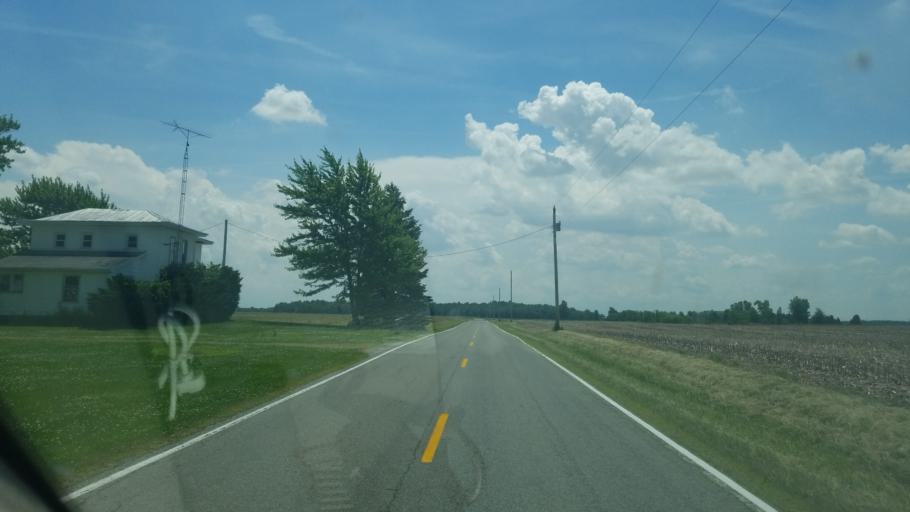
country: US
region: Ohio
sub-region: Hancock County
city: Arlington
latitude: 40.8975
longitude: -83.5948
